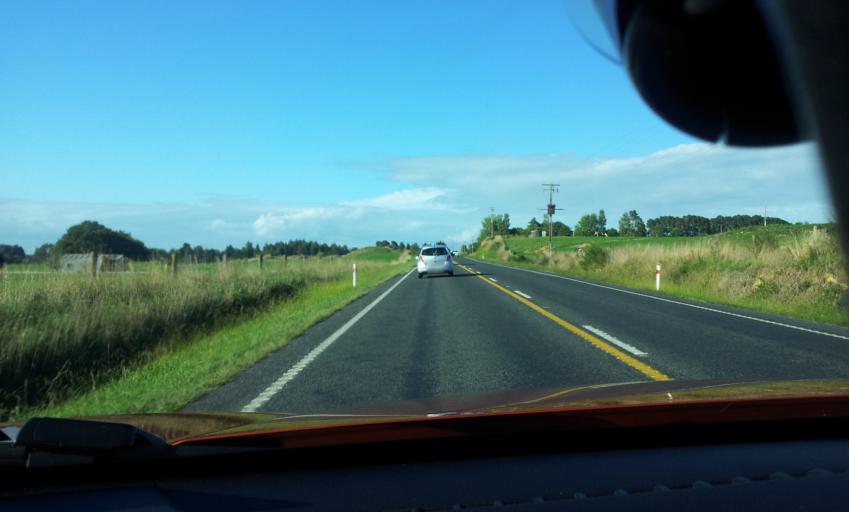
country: NZ
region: Waikato
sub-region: Hauraki District
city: Ngatea
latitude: -37.4671
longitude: 175.5100
